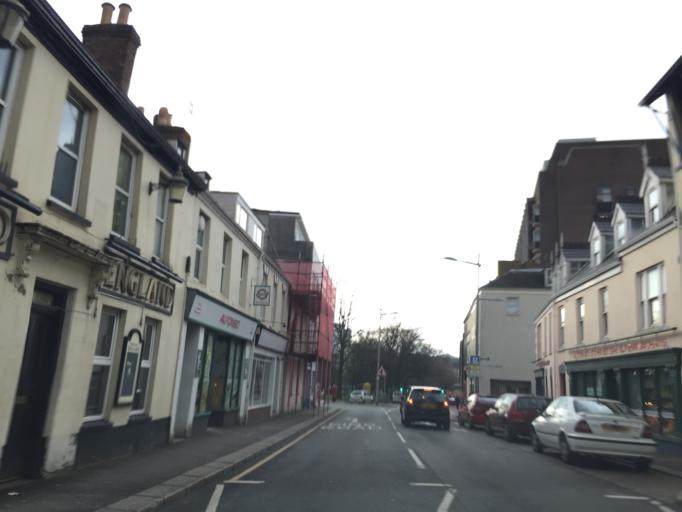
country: JE
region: St Helier
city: Saint Helier
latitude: 49.1890
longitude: -2.1127
